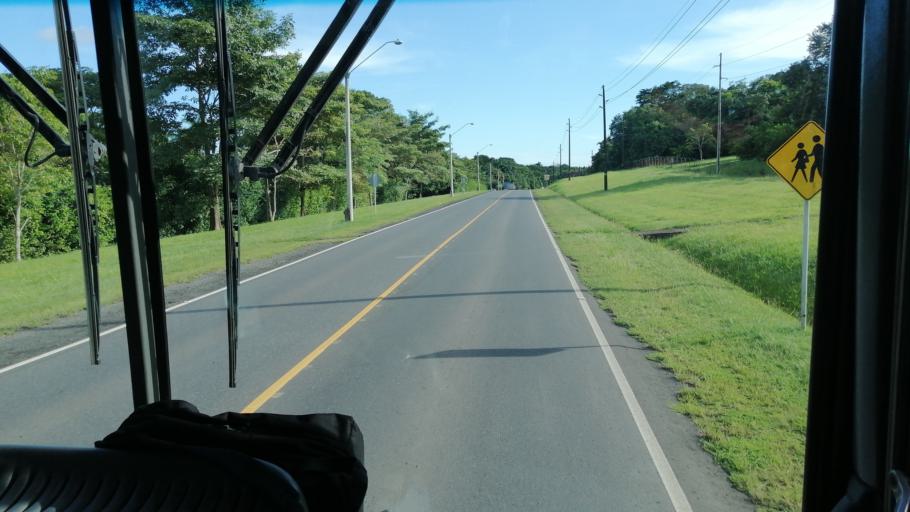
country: PA
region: Panama
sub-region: Distrito de Panama
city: Ancon
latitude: 8.9378
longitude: -79.5910
